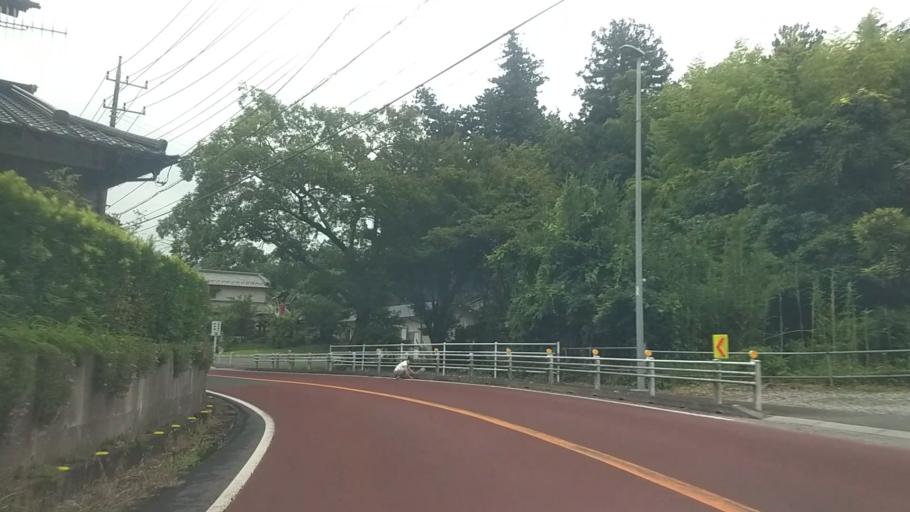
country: JP
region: Chiba
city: Kisarazu
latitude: 35.2899
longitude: 140.0830
